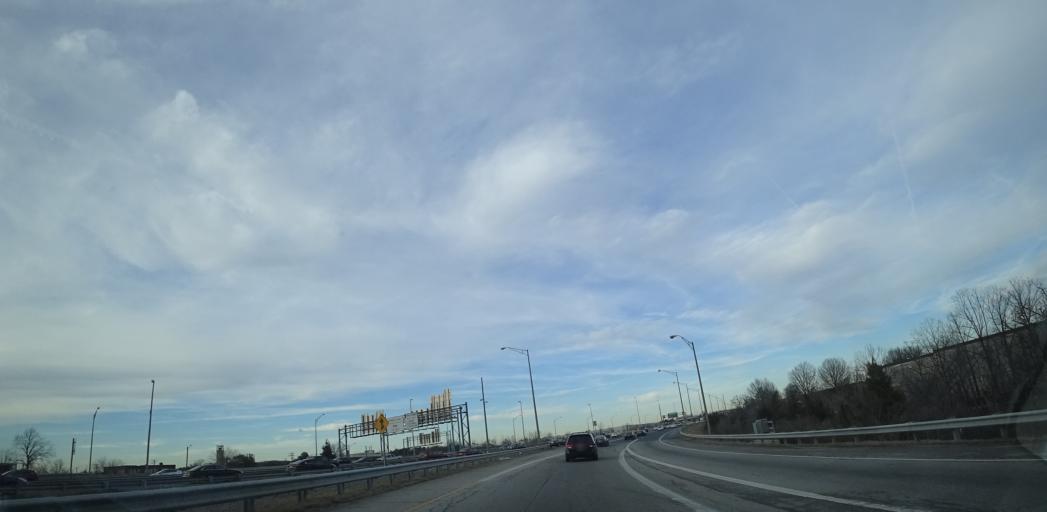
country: US
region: Virginia
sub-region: Fairfax County
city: Springfield
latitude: 38.7935
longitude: -77.1718
